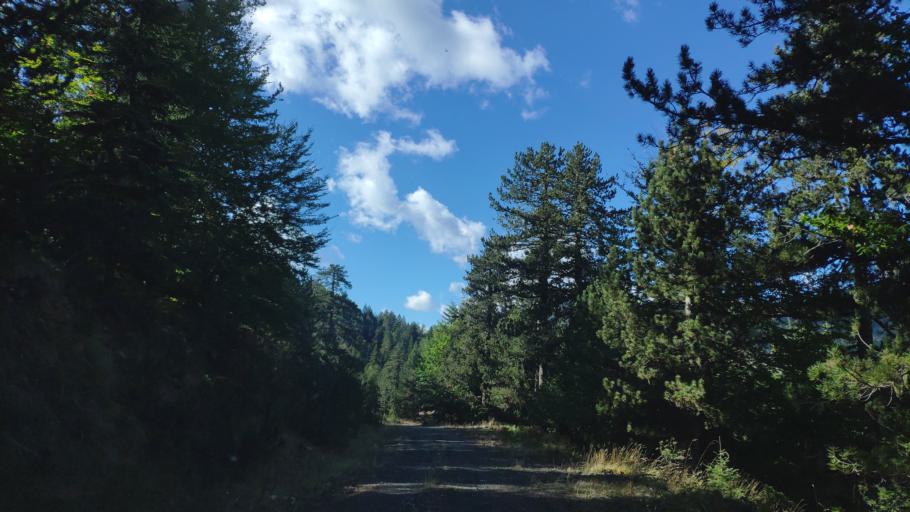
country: GR
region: Epirus
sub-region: Nomos Ioanninon
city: Metsovo
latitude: 39.8937
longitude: 21.2072
